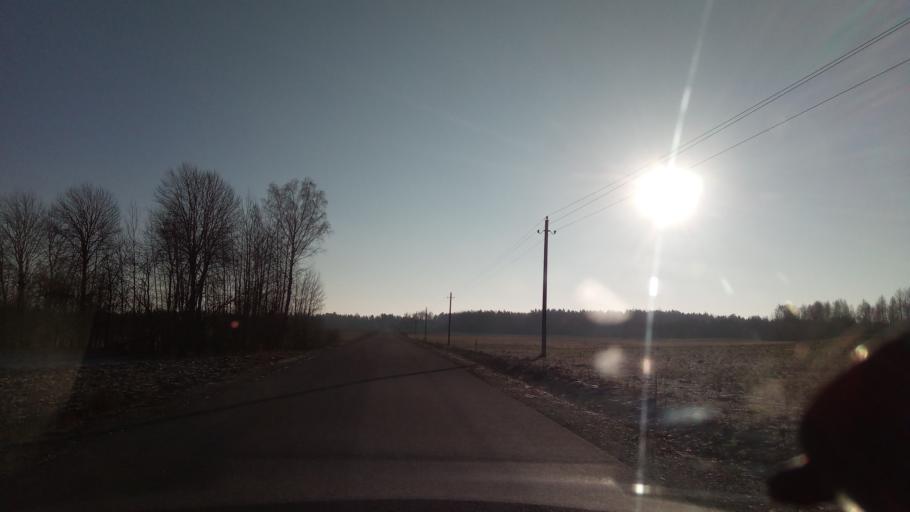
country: LT
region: Alytaus apskritis
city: Druskininkai
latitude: 54.1392
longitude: 23.9864
